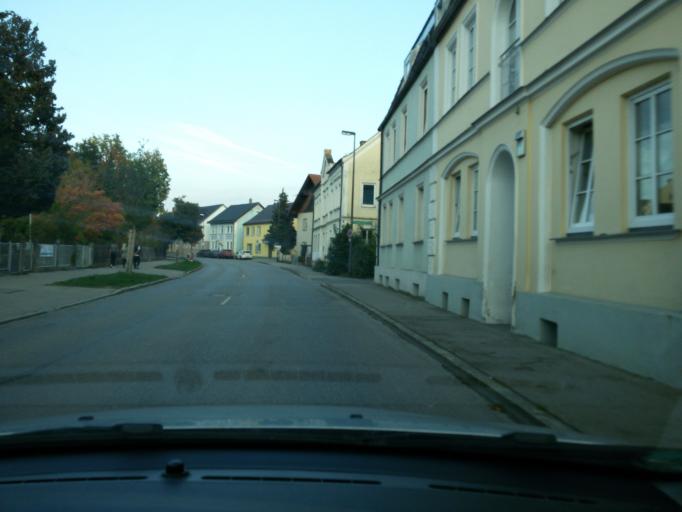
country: DE
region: Bavaria
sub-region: Swabia
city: Mindelheim
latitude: 48.0444
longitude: 10.4861
